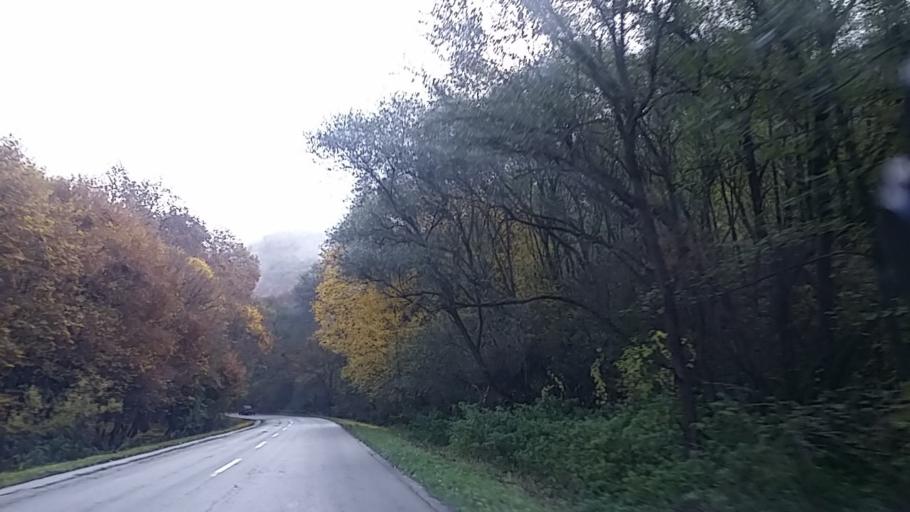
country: HU
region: Heves
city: Belapatfalva
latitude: 48.0043
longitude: 20.3221
